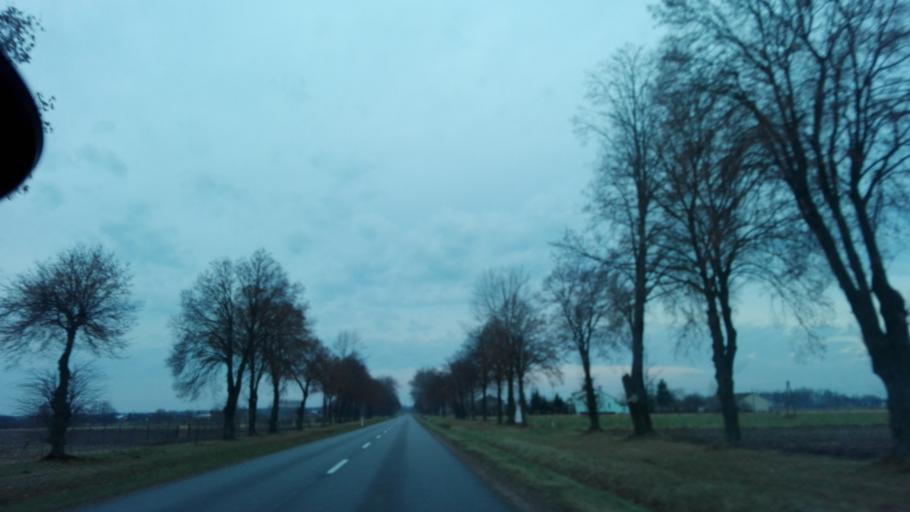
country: PL
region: Lublin Voivodeship
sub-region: Powiat radzynski
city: Wohyn
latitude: 51.7794
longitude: 22.7772
